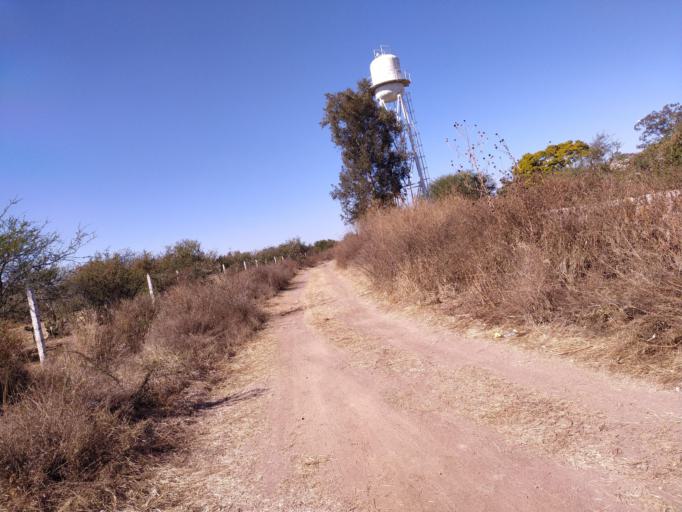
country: MX
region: Guanajuato
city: Ciudad Manuel Doblado
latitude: 20.8114
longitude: -101.9992
